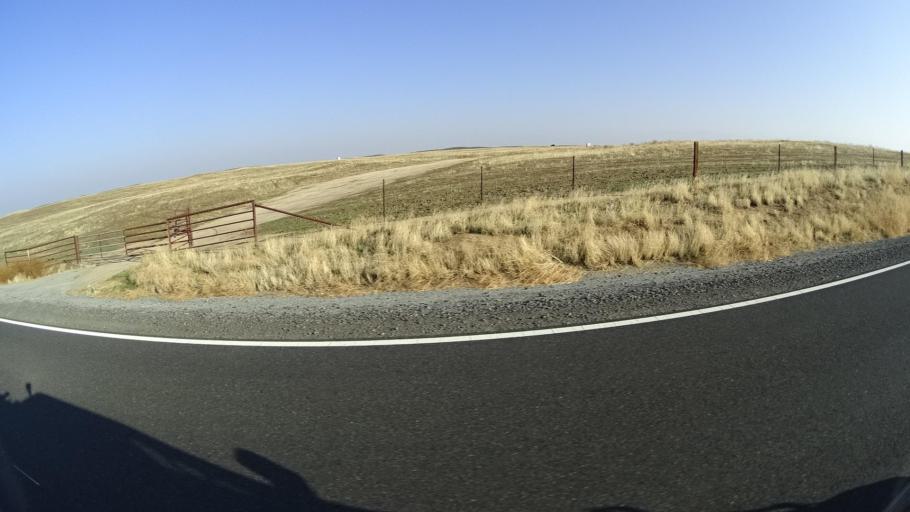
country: US
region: California
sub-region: Tulare County
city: Richgrove
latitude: 35.7500
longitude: -118.9943
